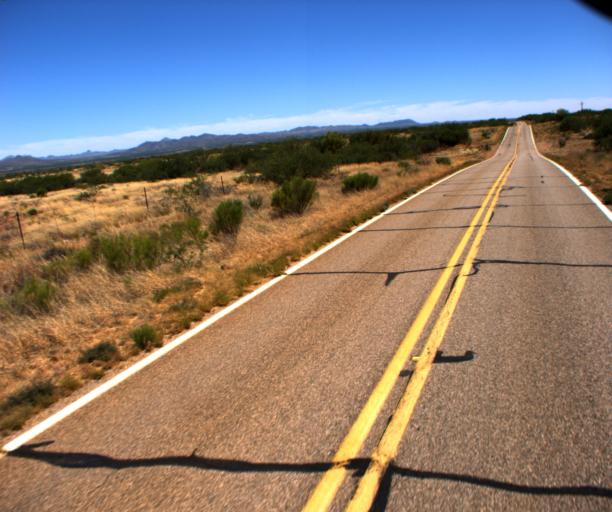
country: US
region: Arizona
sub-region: Pima County
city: Three Points
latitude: 31.7121
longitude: -111.4878
